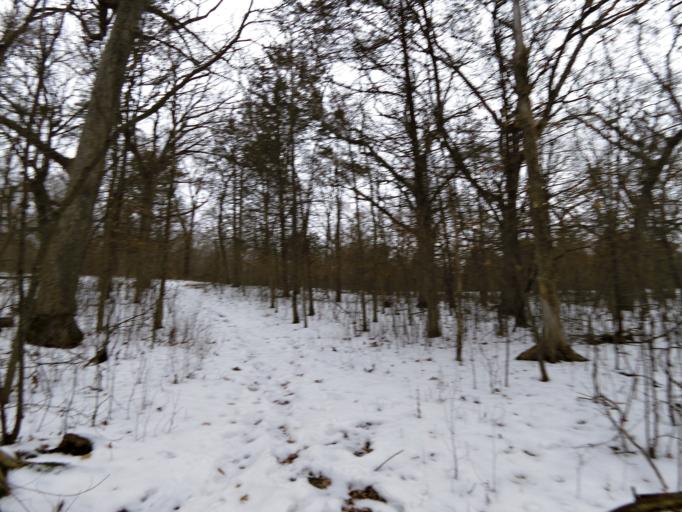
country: US
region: Wisconsin
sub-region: Pierce County
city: Prescott
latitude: 44.8020
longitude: -92.7879
